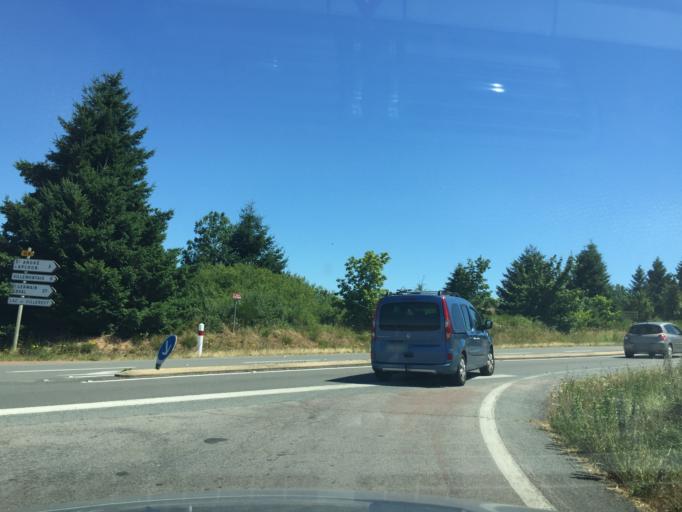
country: FR
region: Rhone-Alpes
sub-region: Departement de la Loire
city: Renaison
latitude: 46.0404
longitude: 3.9319
